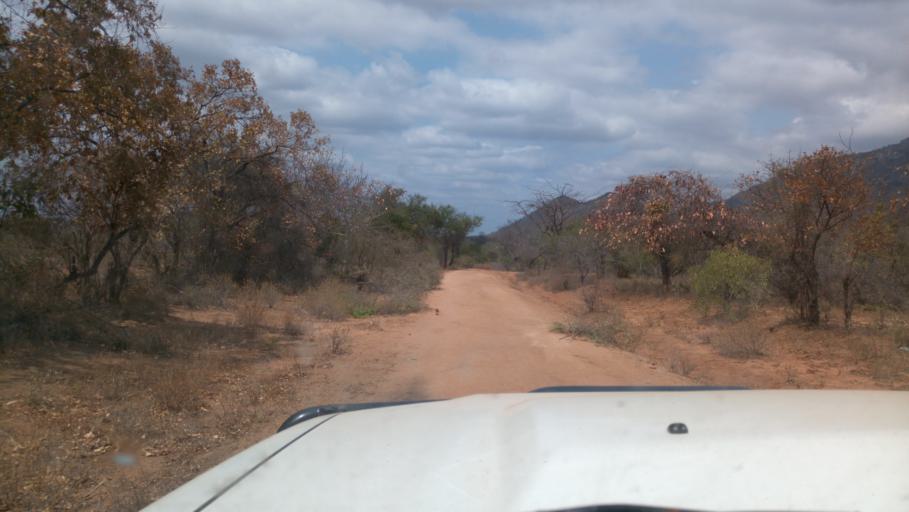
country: KE
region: Kitui
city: Kitui
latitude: -1.8720
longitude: 38.3693
